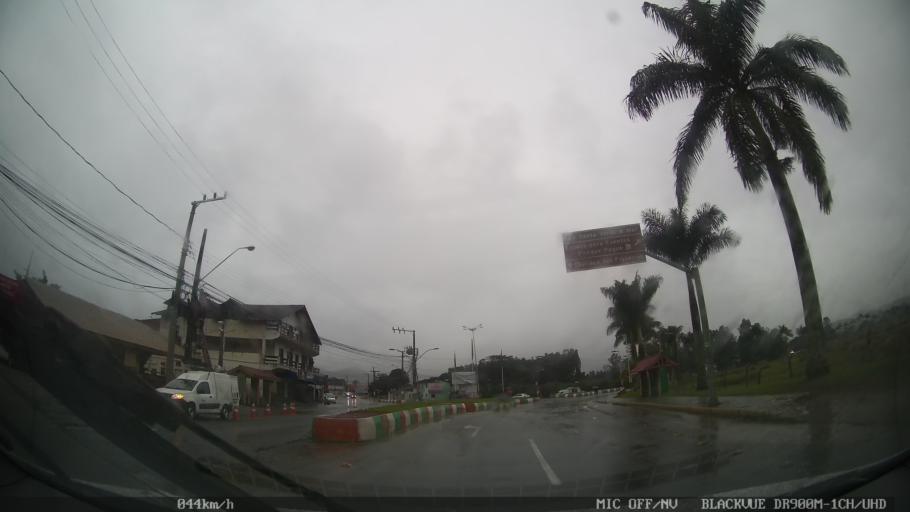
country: BR
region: Santa Catarina
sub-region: Balneario Camboriu
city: Balneario Camboriu
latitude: -27.0170
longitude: -48.6528
